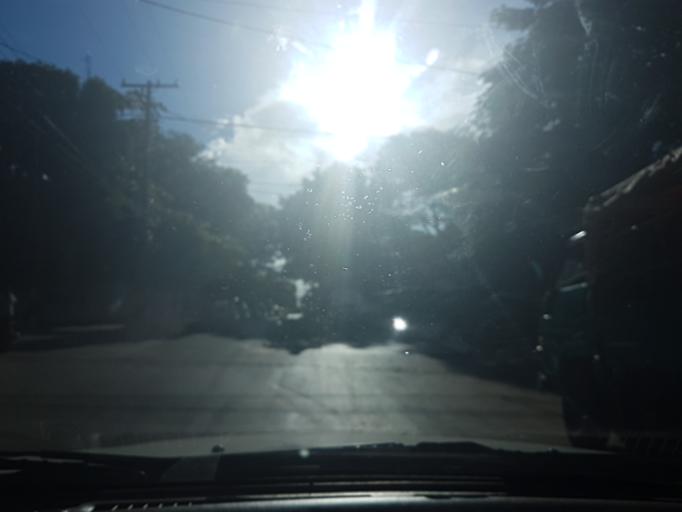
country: PY
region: Central
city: San Lorenzo
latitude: -25.2706
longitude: -57.4906
